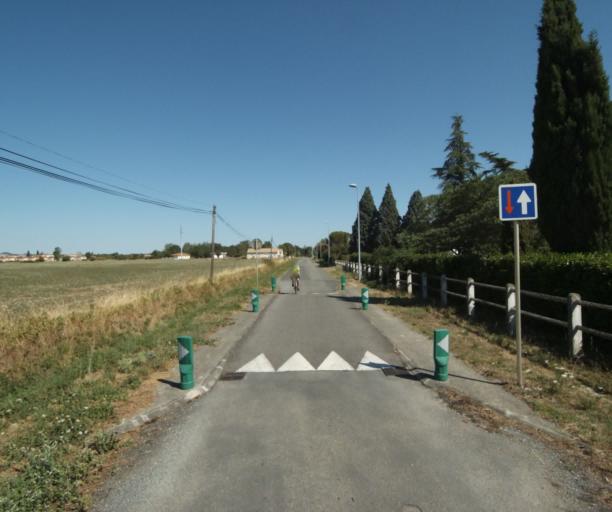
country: FR
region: Midi-Pyrenees
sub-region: Departement de la Haute-Garonne
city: Revel
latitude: 43.4663
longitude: 1.9986
